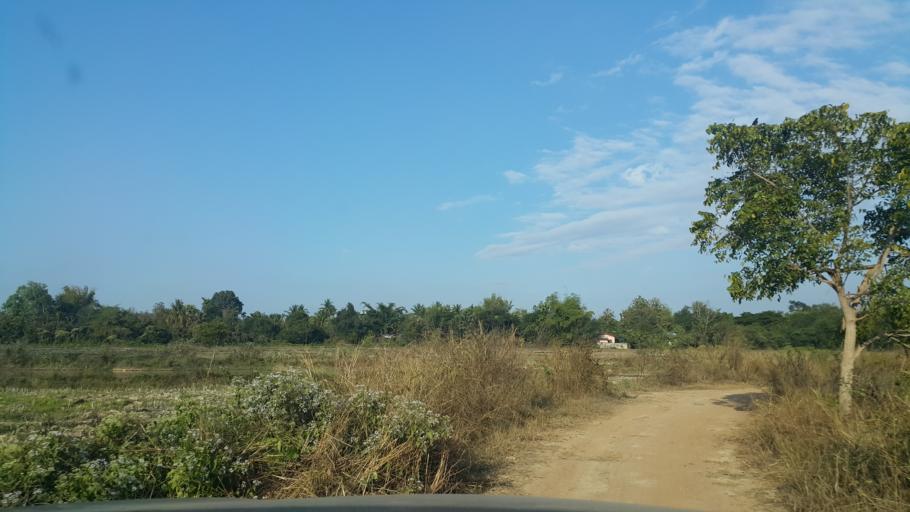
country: TH
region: Lampang
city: Ko Kha
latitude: 18.2258
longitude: 99.3539
